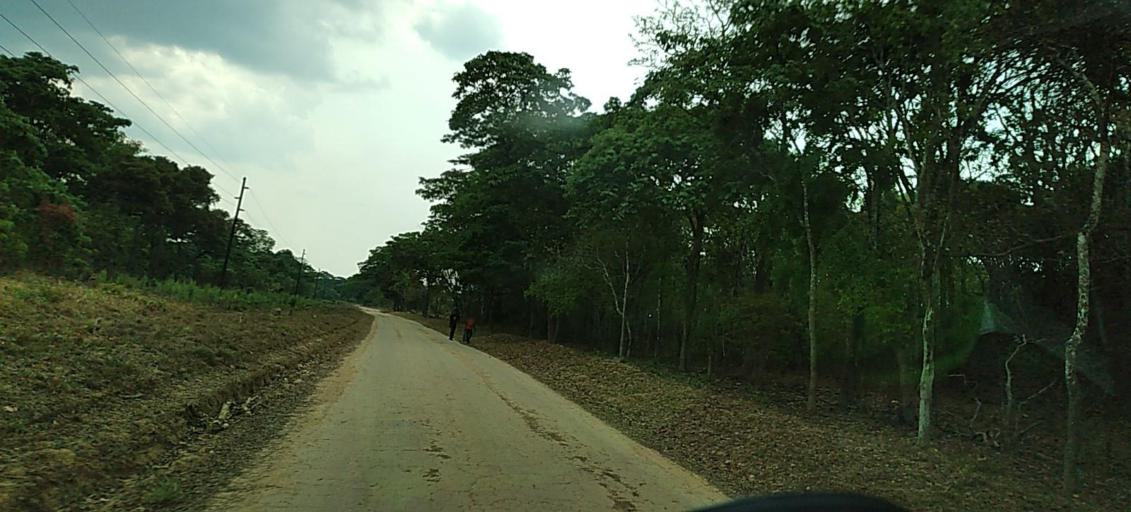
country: ZM
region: North-Western
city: Solwezi
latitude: -12.7726
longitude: 26.4678
